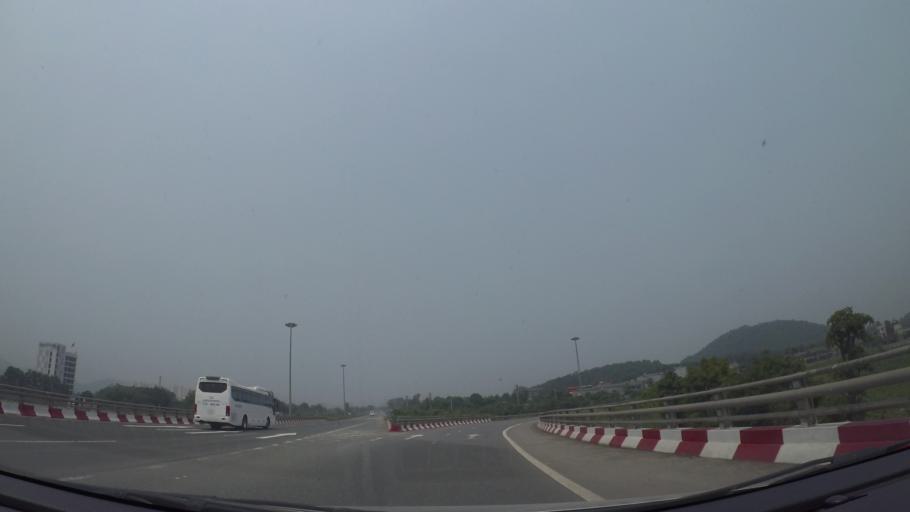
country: VN
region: Ha Noi
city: Lien Quan
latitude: 20.9906
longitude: 105.5233
